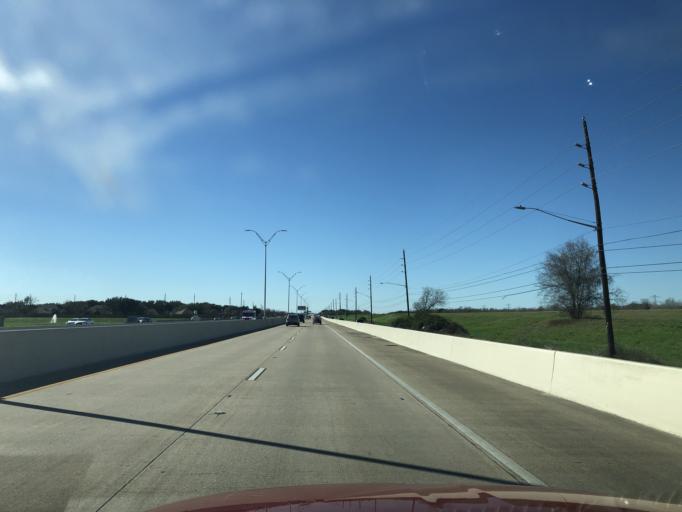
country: US
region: Texas
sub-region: Fort Bend County
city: Mission Bend
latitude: 29.7072
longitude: -95.6946
